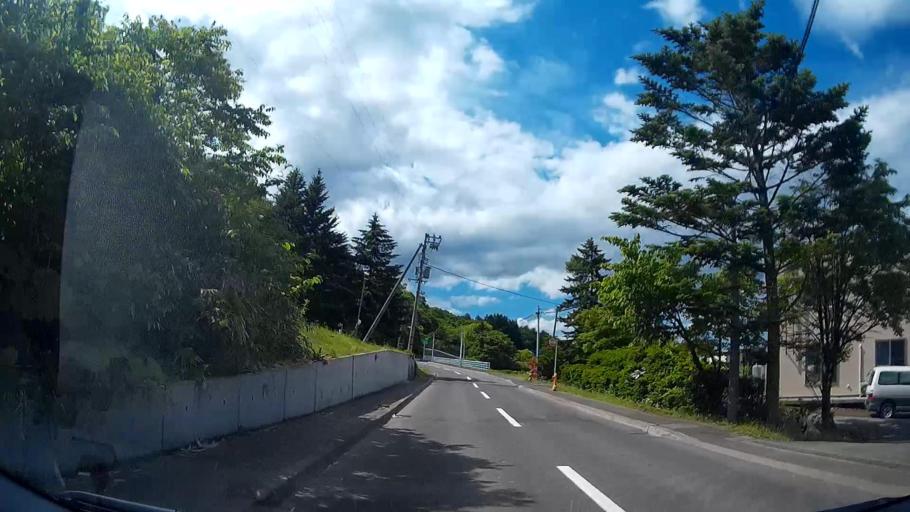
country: JP
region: Hokkaido
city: Sapporo
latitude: 42.9351
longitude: 141.3294
